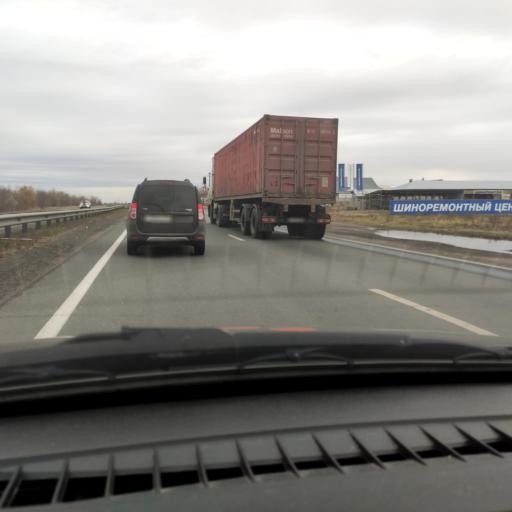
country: RU
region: Samara
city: Tol'yatti
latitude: 53.5645
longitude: 49.3685
